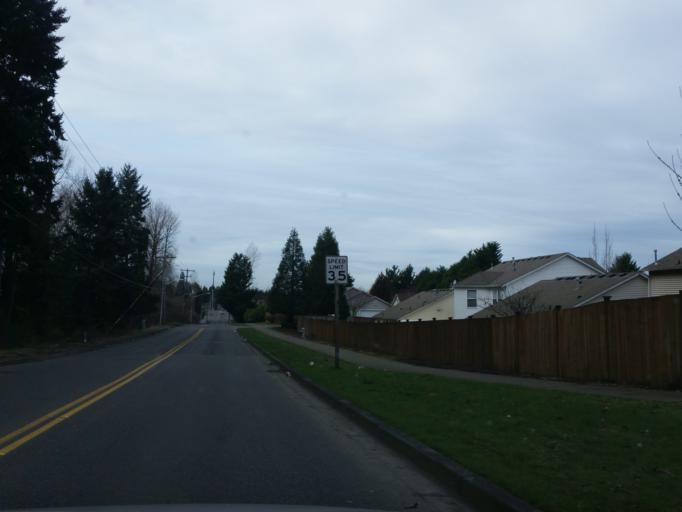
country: US
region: Washington
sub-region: Pierce County
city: South Hill
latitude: 47.1328
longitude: -122.2673
